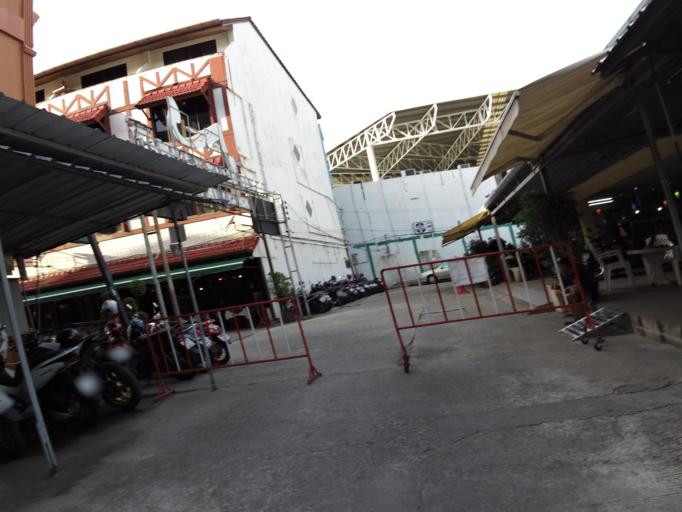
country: TH
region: Phuket
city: Patong
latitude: 7.8946
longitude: 98.2964
